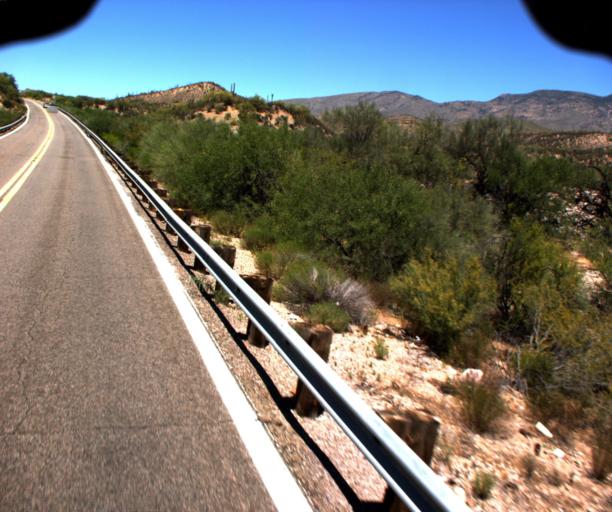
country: US
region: Arizona
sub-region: Pinal County
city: Kearny
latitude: 33.1267
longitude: -110.7762
